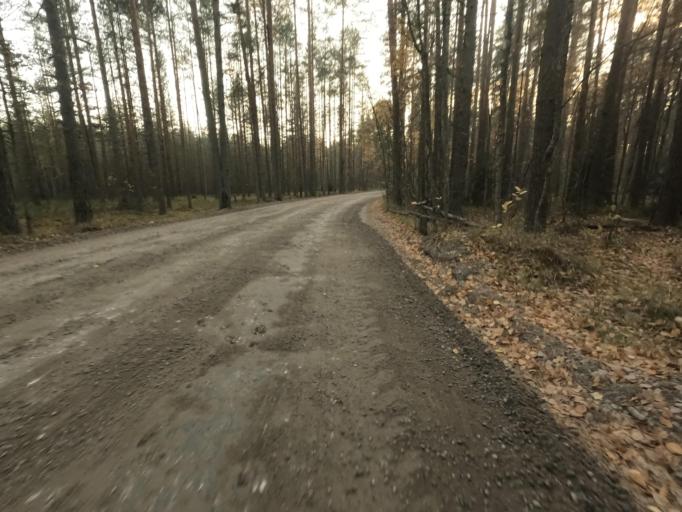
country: RU
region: St.-Petersburg
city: Repino
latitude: 60.1883
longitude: 29.8796
